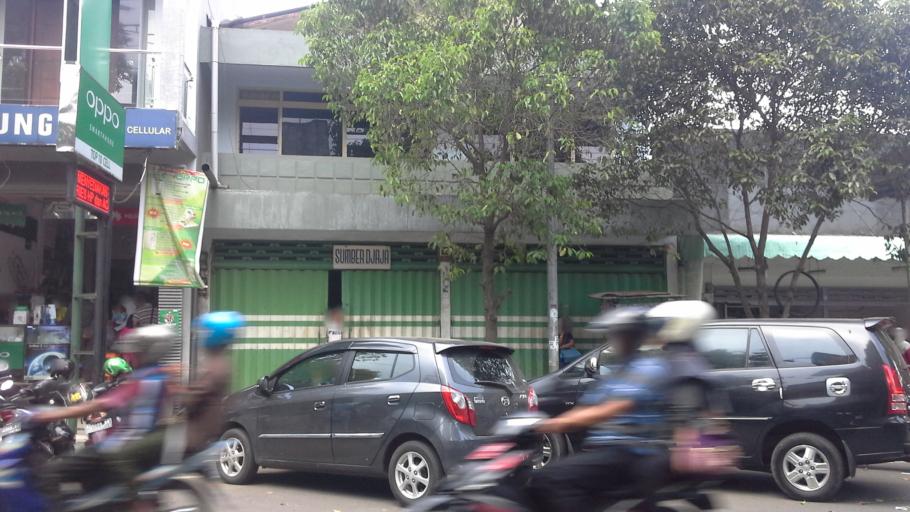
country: ID
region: East Java
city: Bondowoso
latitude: -7.9150
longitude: 113.8267
